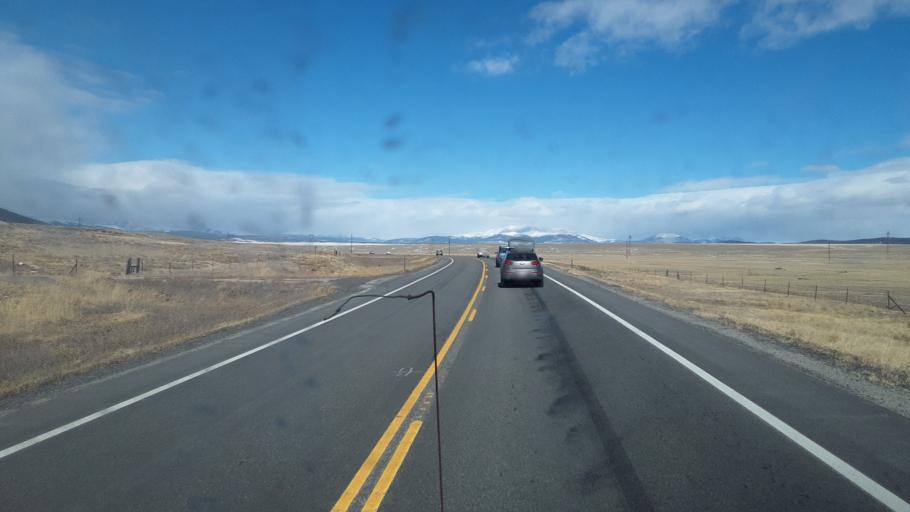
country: US
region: Colorado
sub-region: Park County
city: Fairplay
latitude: 39.0767
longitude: -105.9736
